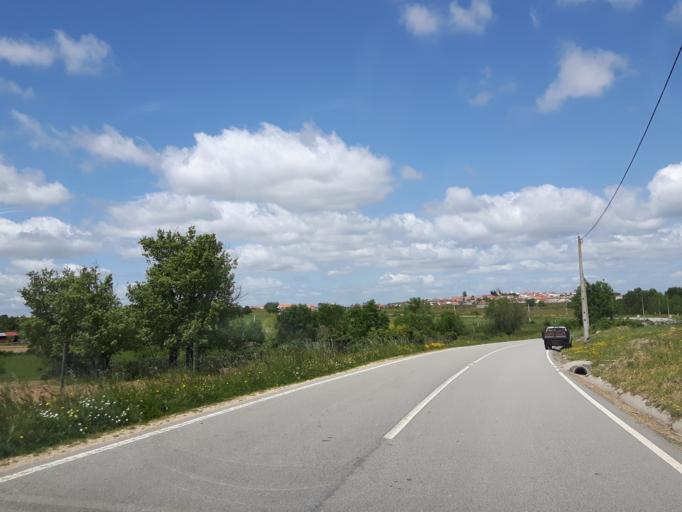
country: ES
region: Castille and Leon
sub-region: Provincia de Salamanca
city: Aldea del Obispo
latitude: 40.7191
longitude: -6.8846
